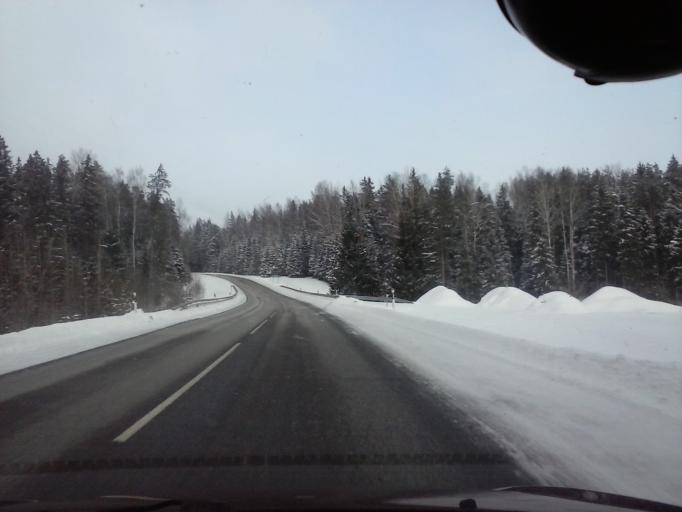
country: EE
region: Paernumaa
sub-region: Saarde vald
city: Kilingi-Nomme
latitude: 58.1819
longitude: 25.0514
